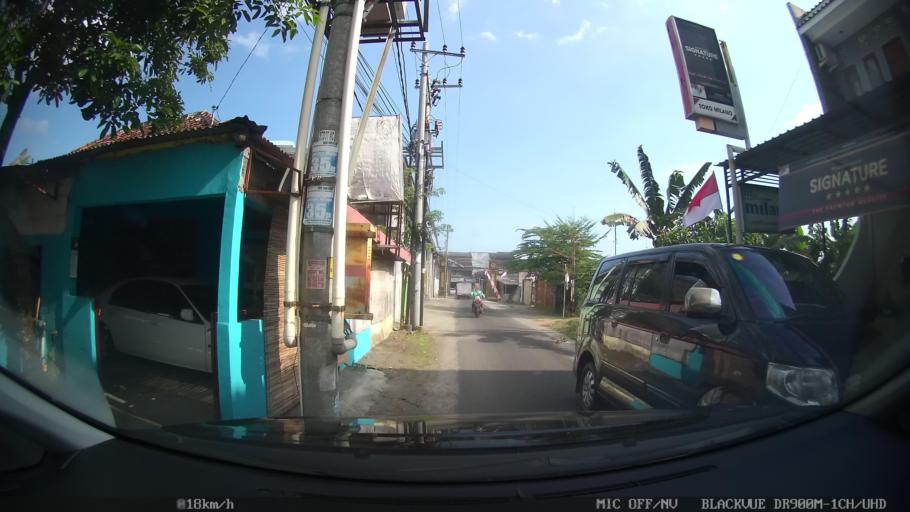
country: ID
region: Daerah Istimewa Yogyakarta
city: Gamping Lor
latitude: -7.7996
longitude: 110.3411
